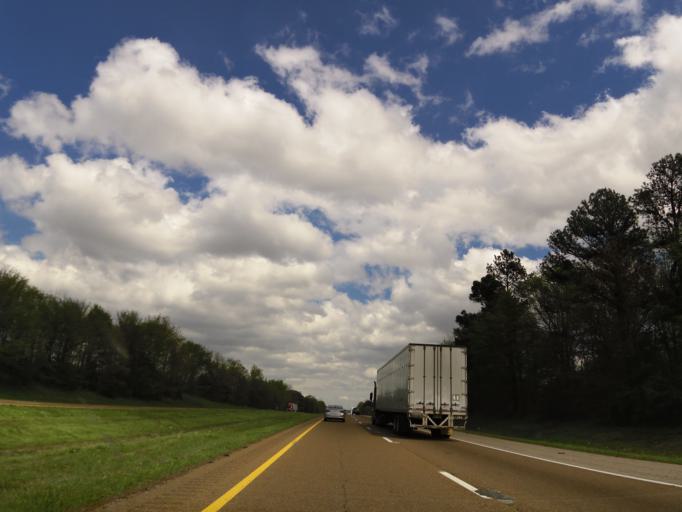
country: US
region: Tennessee
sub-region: Tipton County
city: Mason
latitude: 35.3727
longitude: -89.4658
